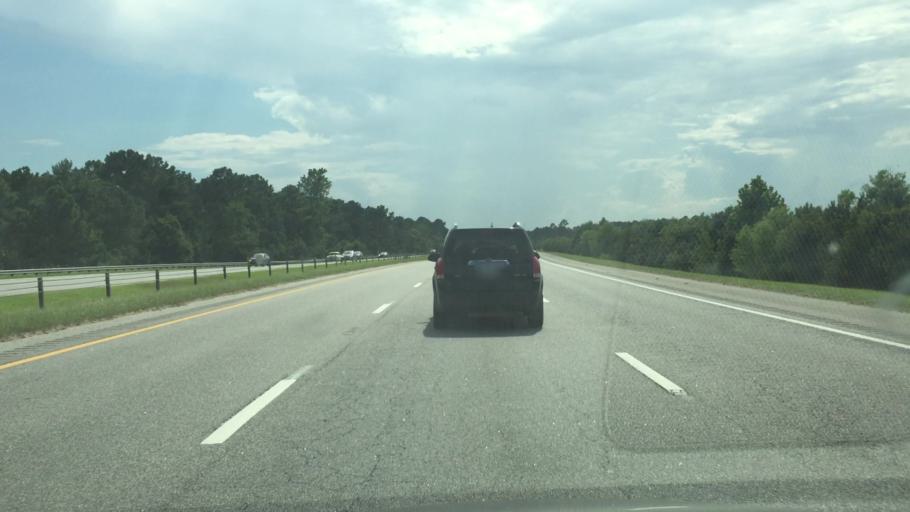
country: US
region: South Carolina
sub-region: Horry County
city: Myrtle Beach
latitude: 33.7716
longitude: -78.8225
